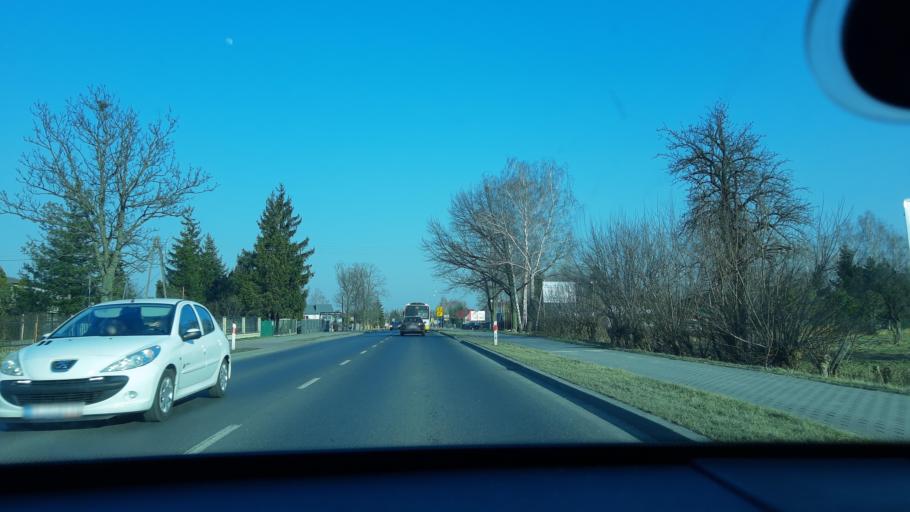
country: PL
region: Lodz Voivodeship
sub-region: Powiat zdunskowolski
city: Zdunska Wola
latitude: 51.6080
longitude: 18.9043
